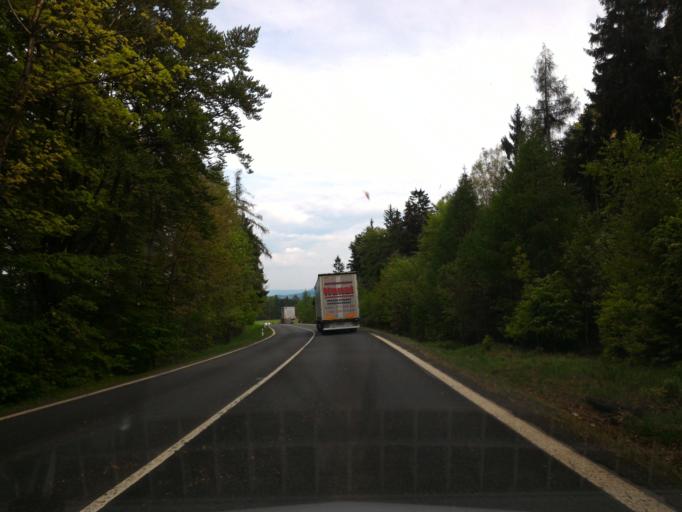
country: CZ
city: Cvikov
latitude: 50.8017
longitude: 14.5932
